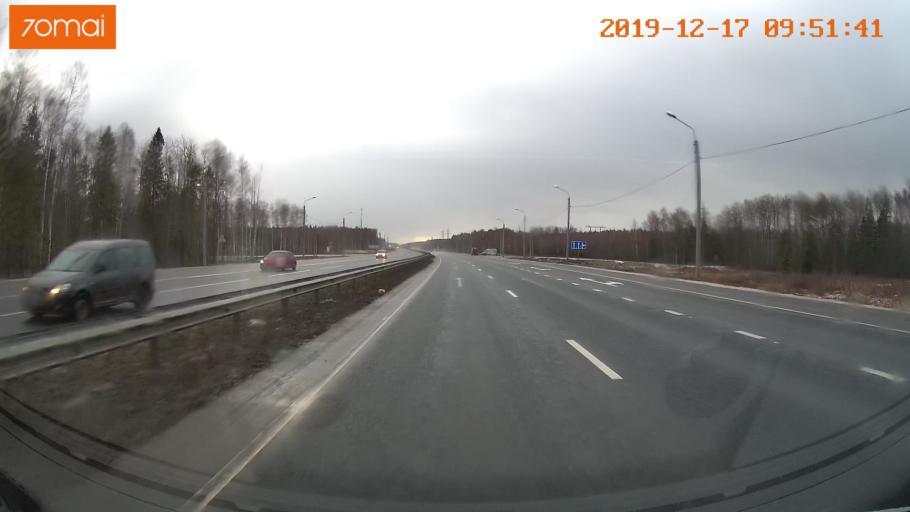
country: RU
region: Vladimir
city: Kommunar
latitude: 56.0411
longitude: 40.5246
